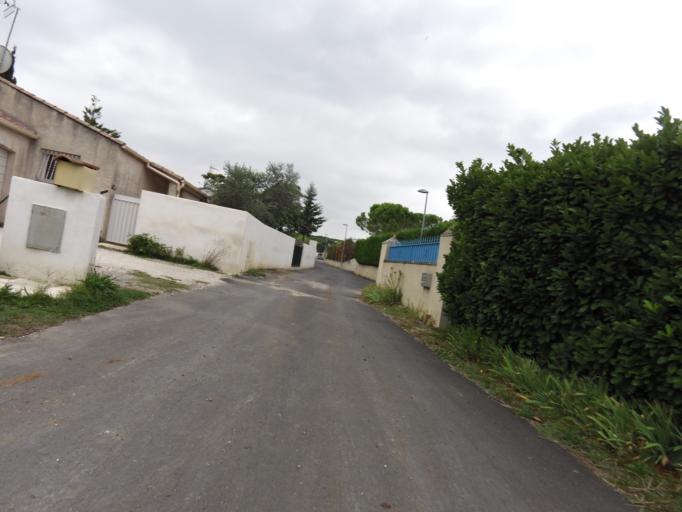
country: FR
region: Languedoc-Roussillon
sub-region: Departement de l'Herault
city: Villetelle
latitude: 43.7242
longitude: 4.1347
